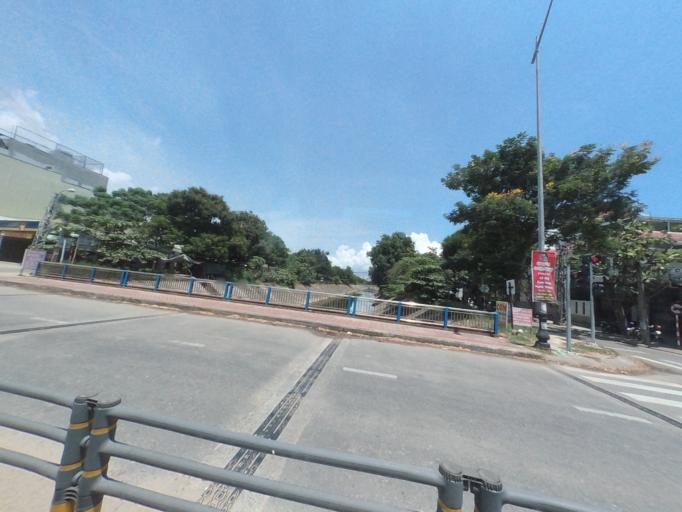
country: VN
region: Da Nang
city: Lien Chieu
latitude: 16.0716
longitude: 108.1732
